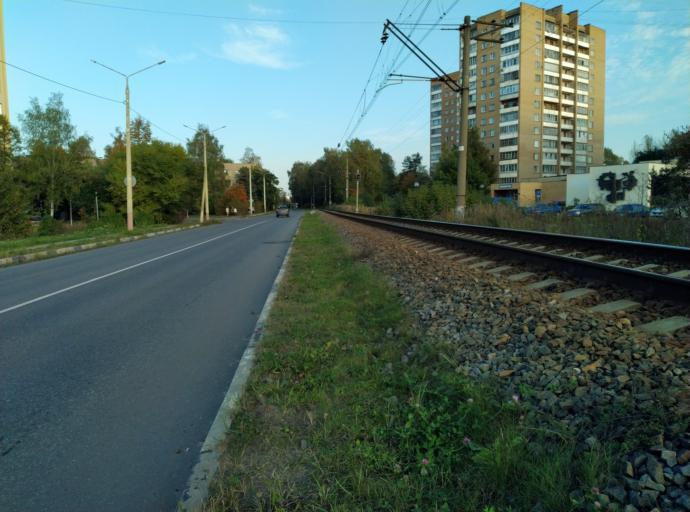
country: RU
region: Moskovskaya
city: Dubna
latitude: 56.7435
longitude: 37.1731
